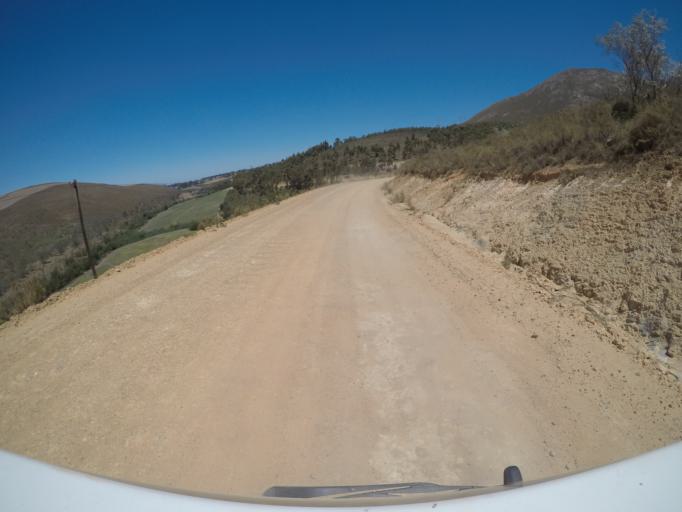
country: ZA
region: Western Cape
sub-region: Overberg District Municipality
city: Grabouw
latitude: -34.2065
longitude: 19.2155
